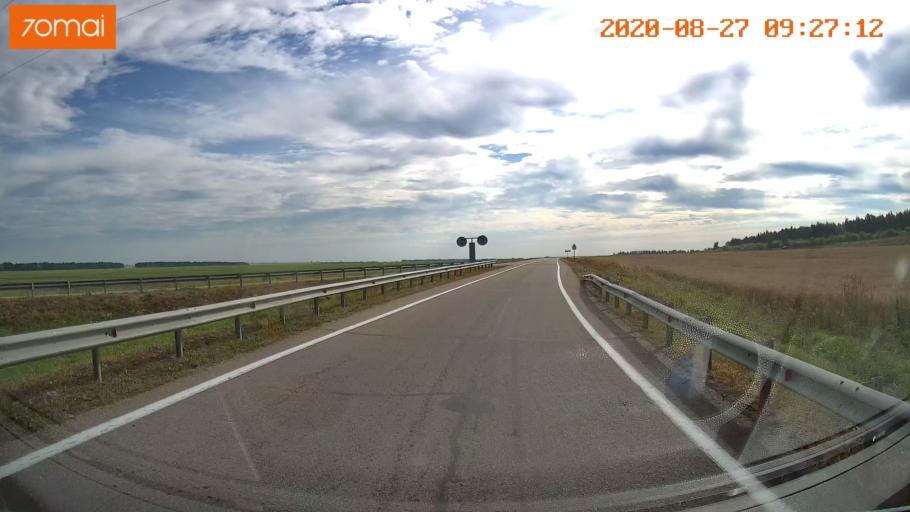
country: RU
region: Tula
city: Kazachka
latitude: 53.3143
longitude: 38.1811
